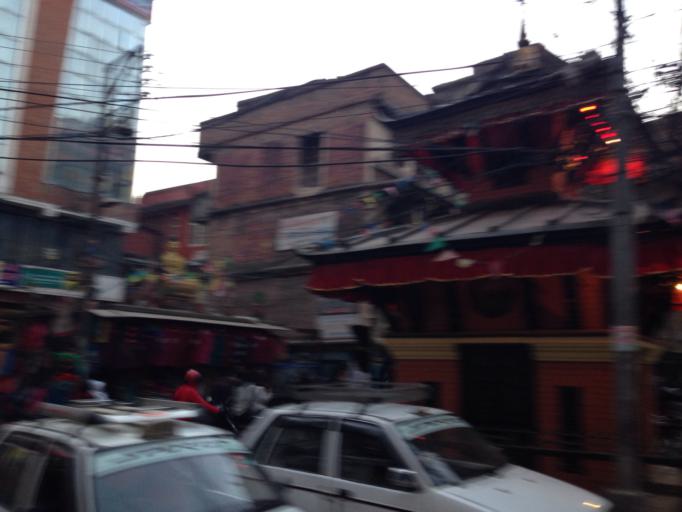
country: NP
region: Central Region
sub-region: Bagmati Zone
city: Kathmandu
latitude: 27.7107
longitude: 85.3097
